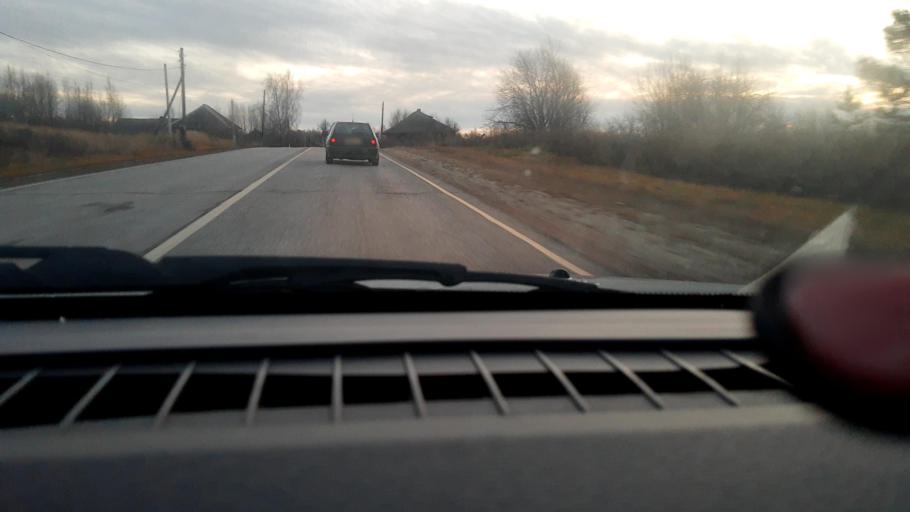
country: RU
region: Nizjnij Novgorod
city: Krasnyye Baki
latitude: 57.0153
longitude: 45.1159
